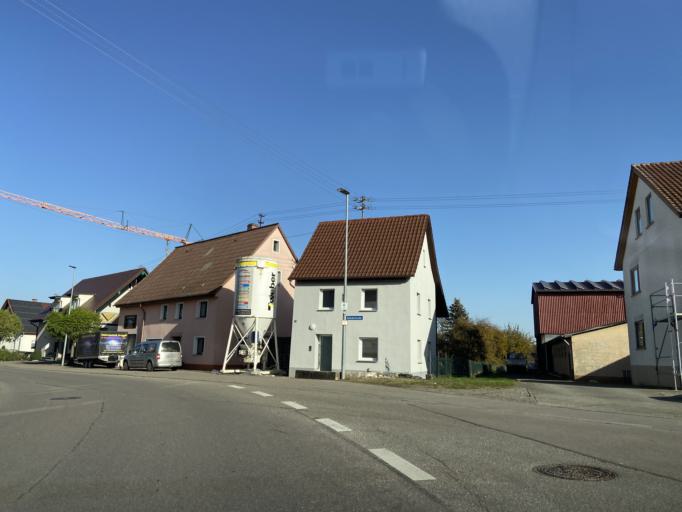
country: DE
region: Baden-Wuerttemberg
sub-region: Tuebingen Region
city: Ennetach
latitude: 48.0292
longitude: 9.2975
